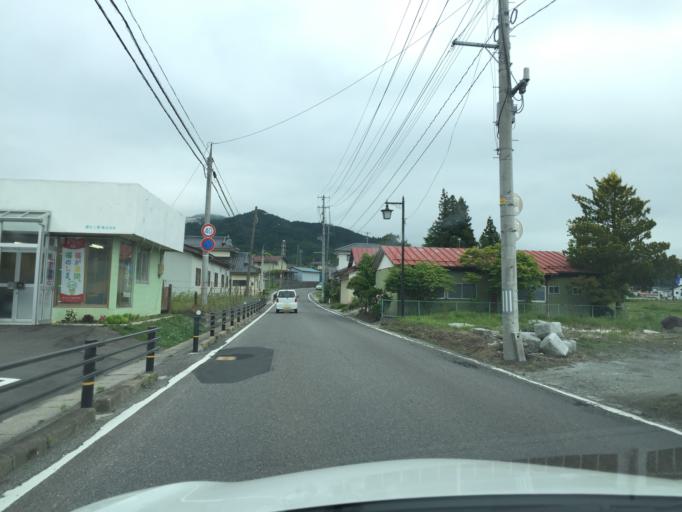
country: JP
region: Fukushima
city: Funehikimachi-funehiki
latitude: 37.3765
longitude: 140.6373
